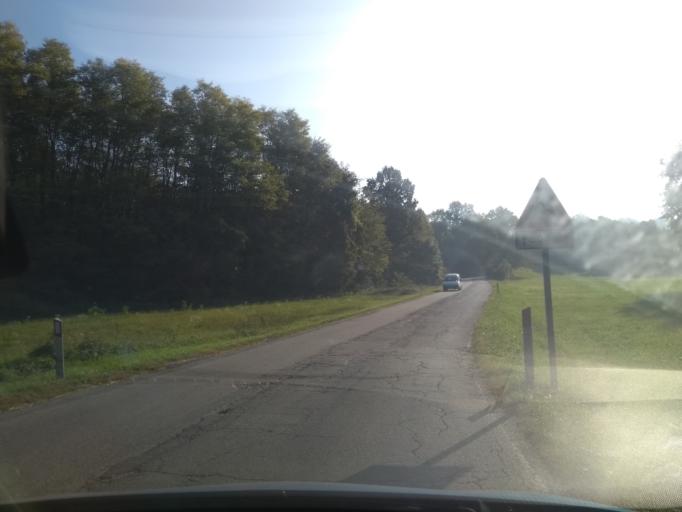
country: IT
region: Piedmont
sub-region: Provincia di Torino
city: Fiano
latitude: 45.2170
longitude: 7.5124
